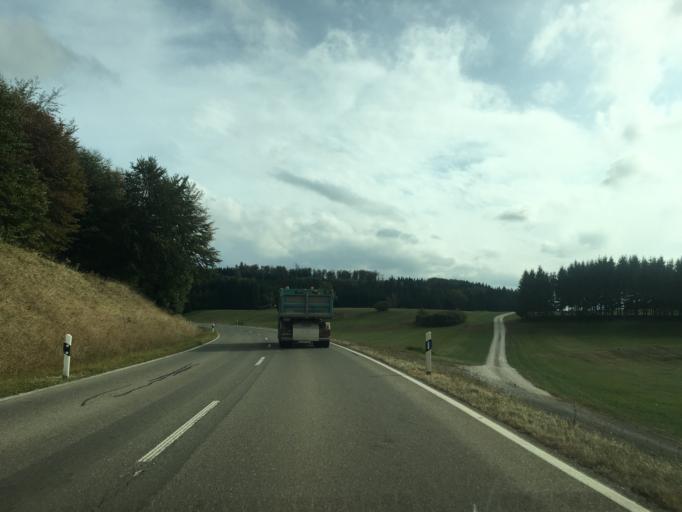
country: DE
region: Baden-Wuerttemberg
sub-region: Tuebingen Region
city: Pfullingen
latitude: 48.3992
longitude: 9.2170
